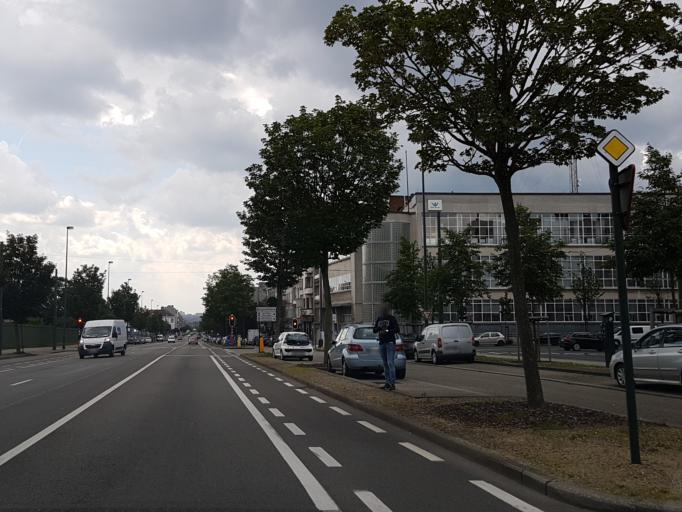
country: BE
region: Flanders
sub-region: Provincie Vlaams-Brabant
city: Bever
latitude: 50.8932
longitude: 4.3330
